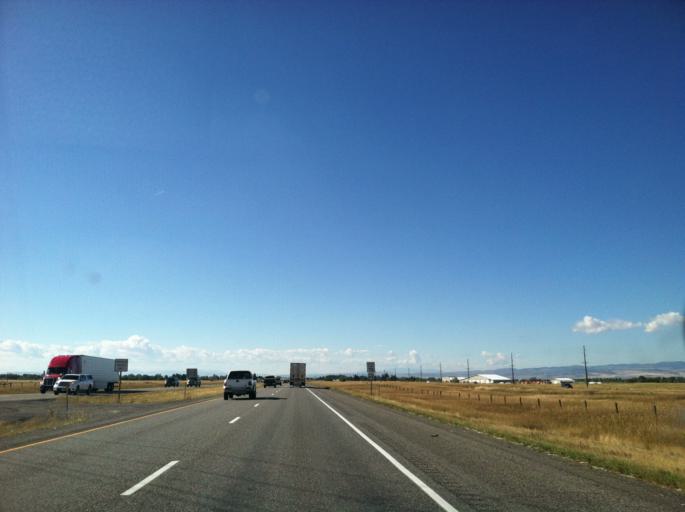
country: US
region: Montana
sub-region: Gallatin County
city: Bozeman
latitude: 45.7227
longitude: -111.0765
